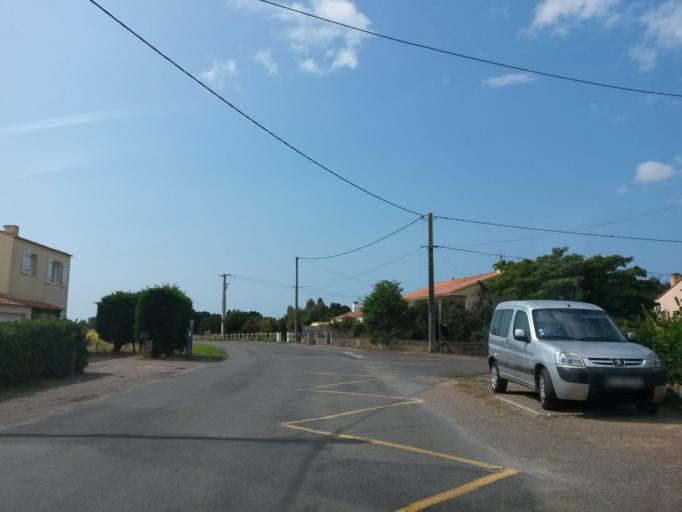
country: FR
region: Pays de la Loire
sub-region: Departement de la Vendee
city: Saint-Hilaire-de-Talmont
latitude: 46.4608
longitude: -1.6161
